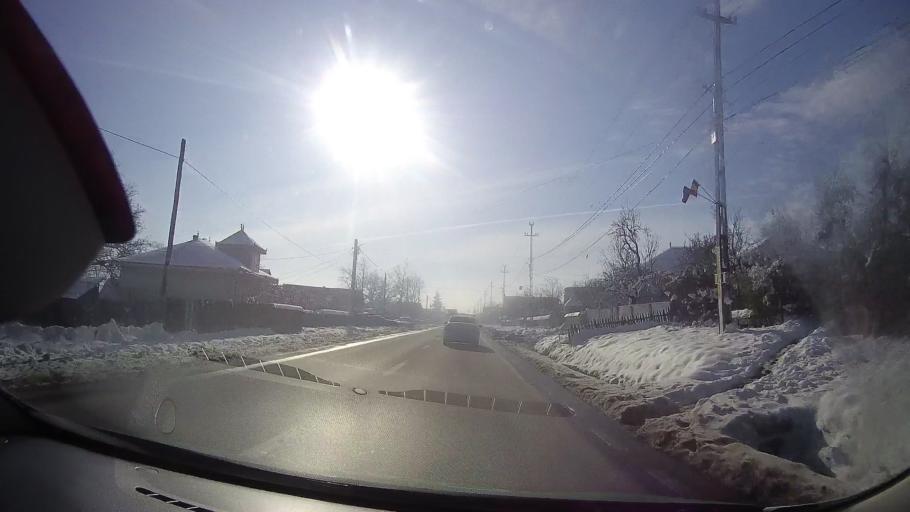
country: RO
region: Iasi
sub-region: Comuna Motca
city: Motca
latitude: 47.2508
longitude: 26.6091
